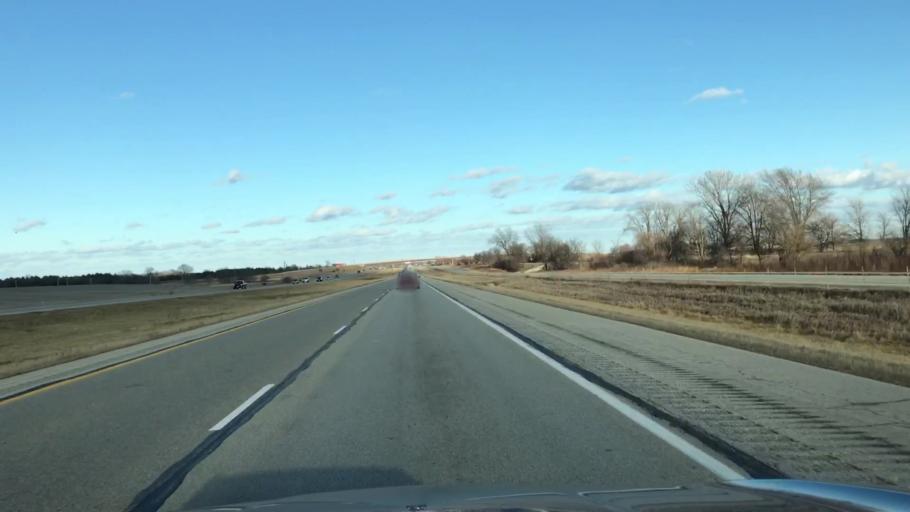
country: US
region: Illinois
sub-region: McLean County
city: Lexington
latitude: 40.5973
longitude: -88.8493
